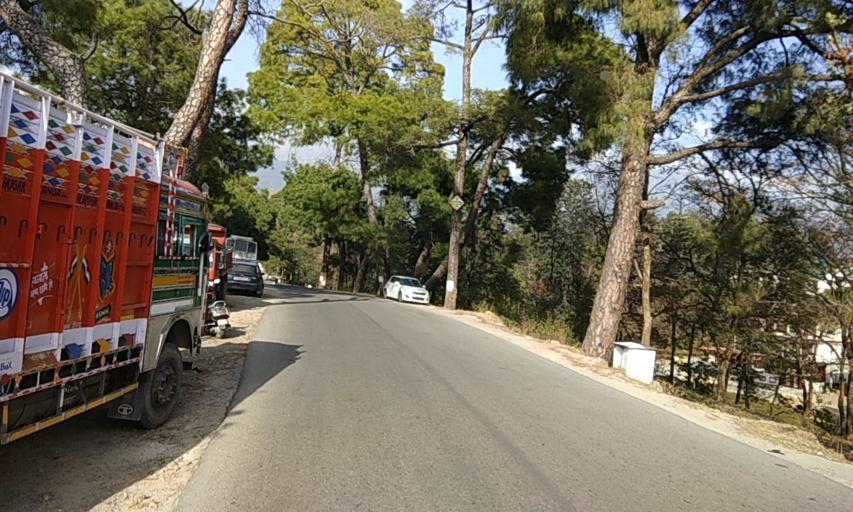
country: IN
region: Himachal Pradesh
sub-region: Kangra
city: Palampur
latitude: 32.0968
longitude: 76.5311
